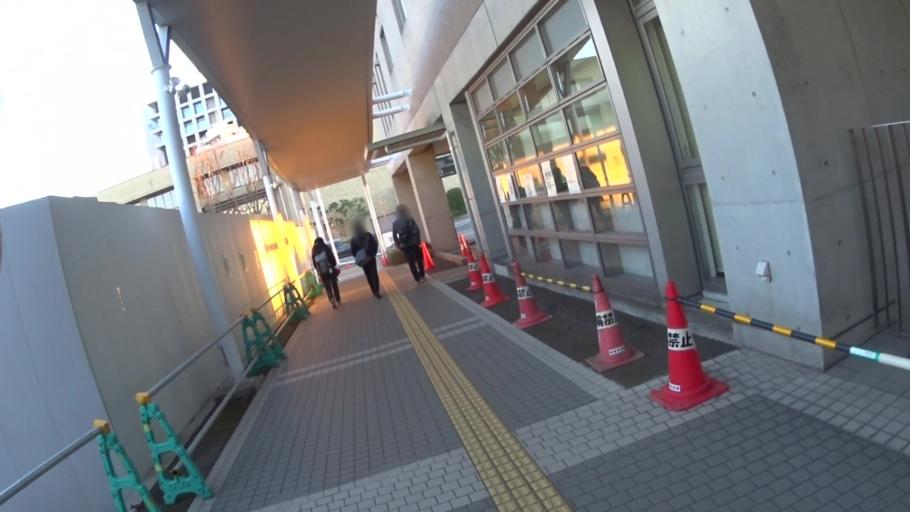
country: JP
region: Tokyo
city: Urayasu
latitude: 35.6548
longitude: 139.9053
